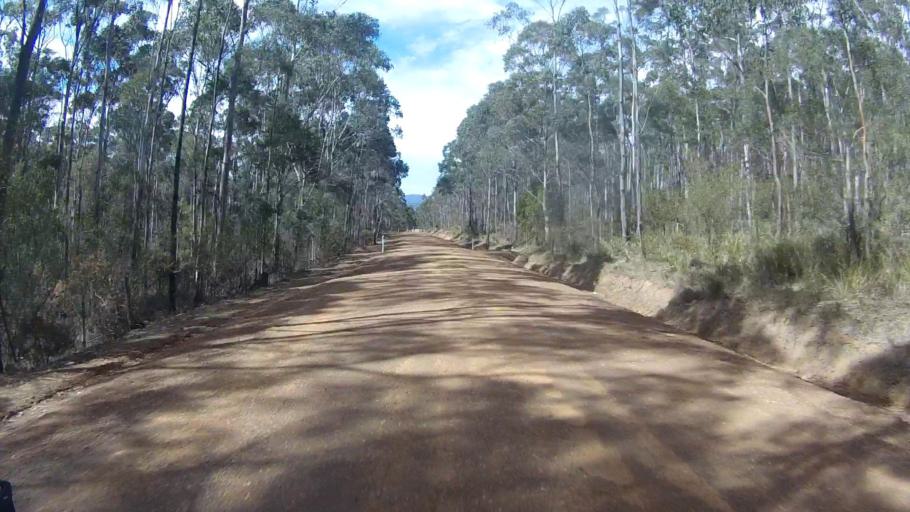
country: AU
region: Tasmania
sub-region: Sorell
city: Sorell
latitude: -42.6254
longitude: 147.9025
